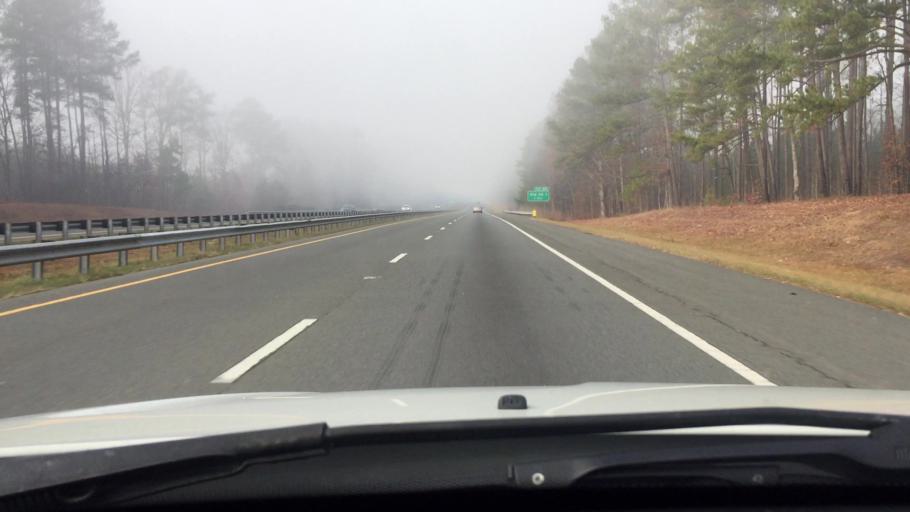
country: US
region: North Carolina
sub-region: Wake County
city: Holly Springs
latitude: 35.6445
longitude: -78.9856
